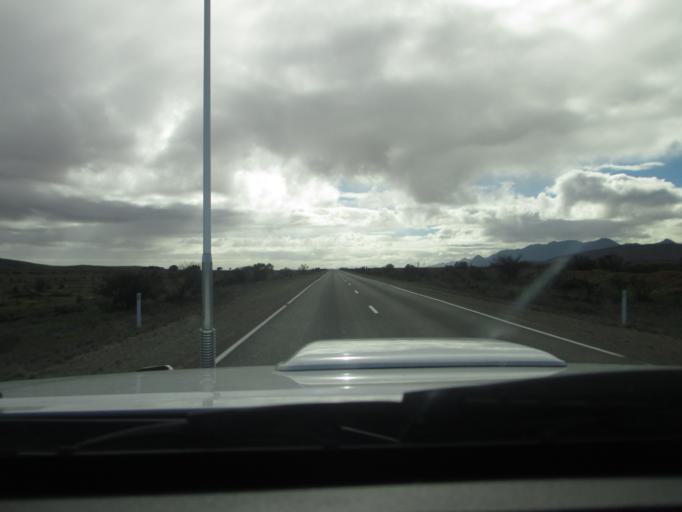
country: AU
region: South Australia
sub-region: Flinders Ranges
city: Quorn
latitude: -31.6345
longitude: 138.3871
